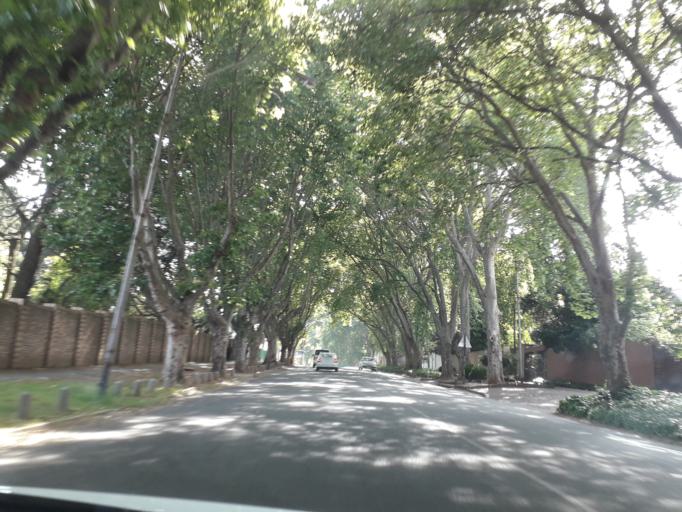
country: ZA
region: Gauteng
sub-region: City of Johannesburg Metropolitan Municipality
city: Johannesburg
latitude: -26.1702
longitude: 28.0360
